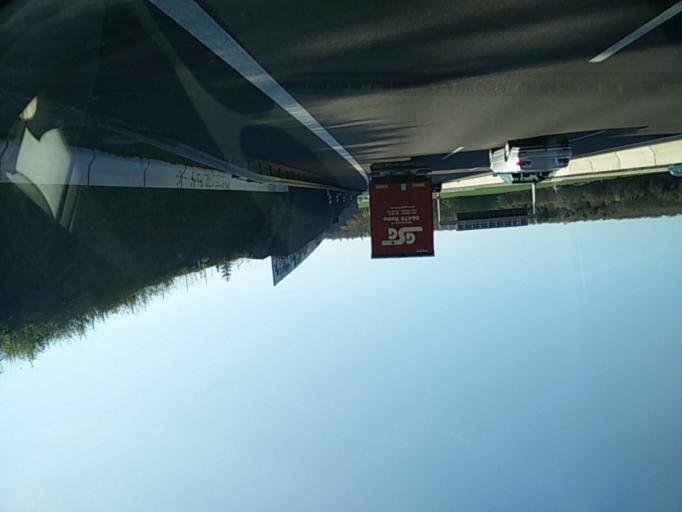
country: DE
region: Baden-Wuerttemberg
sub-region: Regierungsbezirk Stuttgart
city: Ehningen
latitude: 48.6607
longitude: 8.9614
